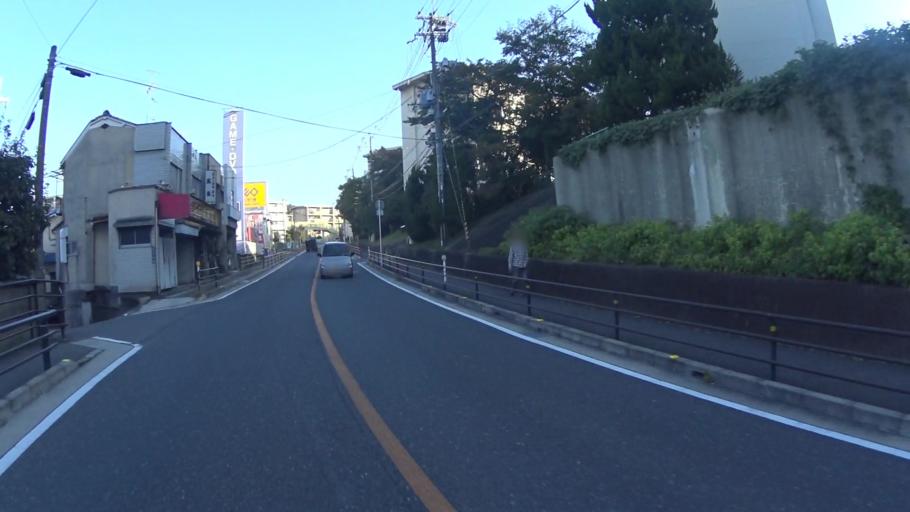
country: JP
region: Kyoto
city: Muko
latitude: 34.9430
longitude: 135.6957
